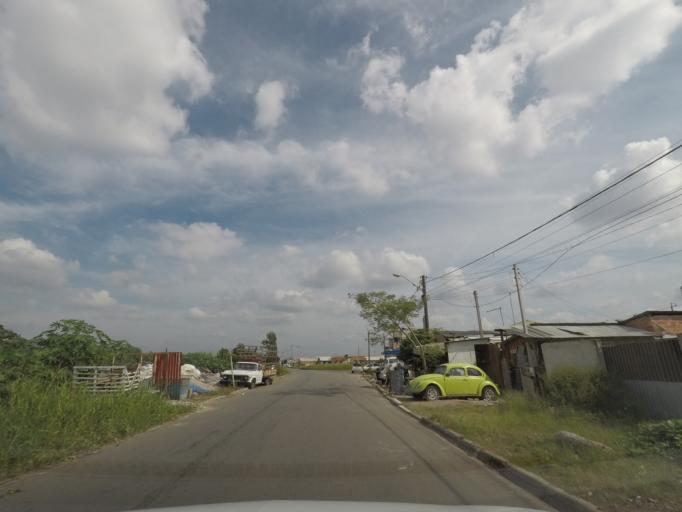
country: BR
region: Parana
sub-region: Sao Jose Dos Pinhais
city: Sao Jose dos Pinhais
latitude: -25.4892
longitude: -49.1968
